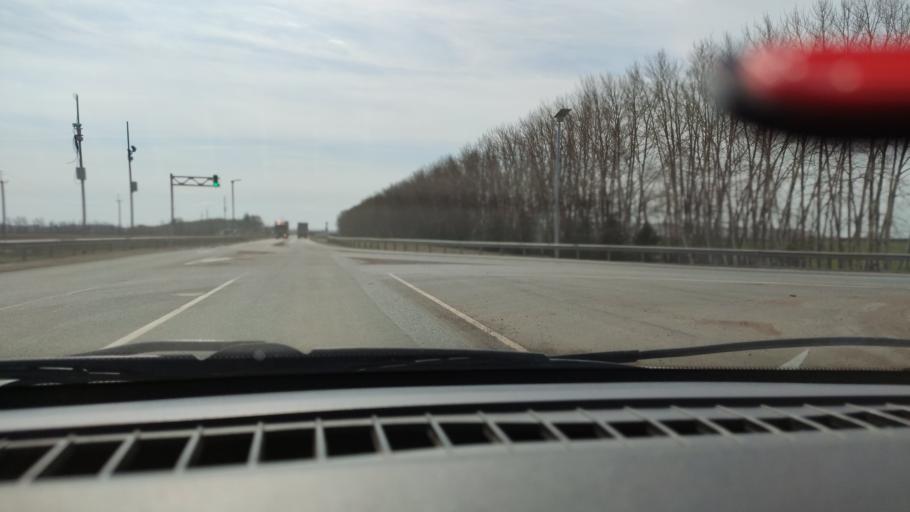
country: RU
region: Bashkortostan
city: Dyurtyuli
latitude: 55.4249
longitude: 54.8073
